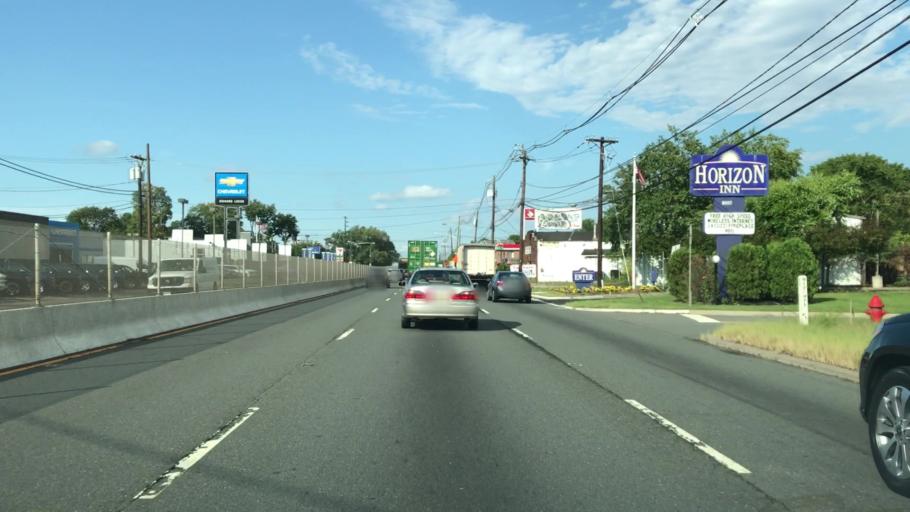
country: US
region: New Jersey
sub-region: Middlesex County
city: Avenel
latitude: 40.5828
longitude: -74.2826
